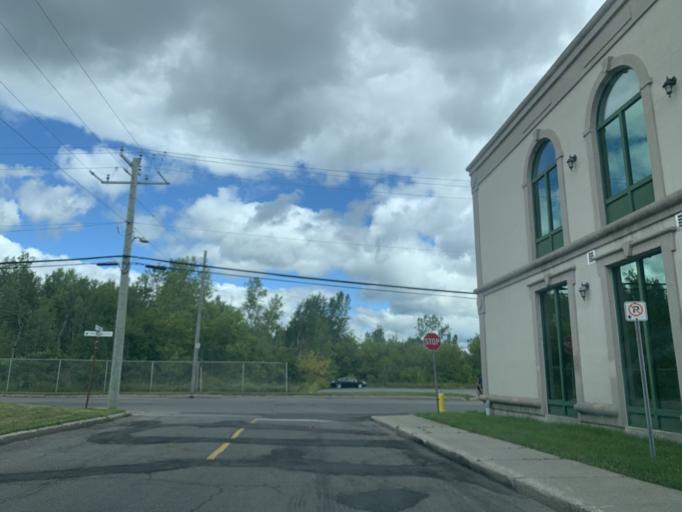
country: CA
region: Ontario
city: Hawkesbury
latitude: 45.6105
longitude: -74.6202
